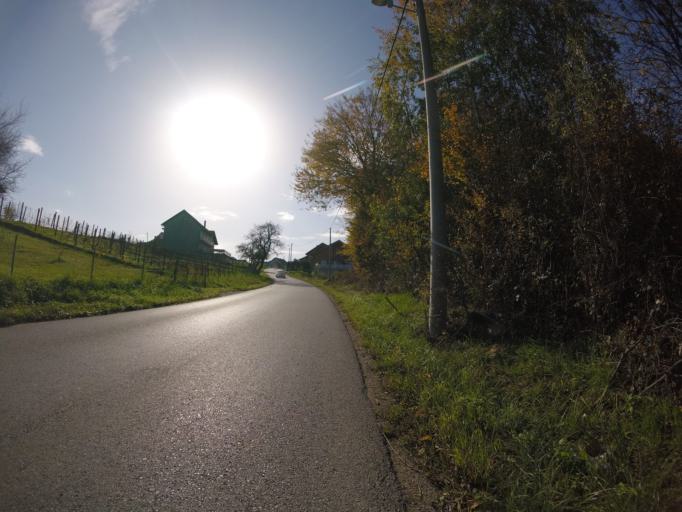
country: HR
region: Zagrebacka
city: Gradici
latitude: 45.6359
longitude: 16.0287
